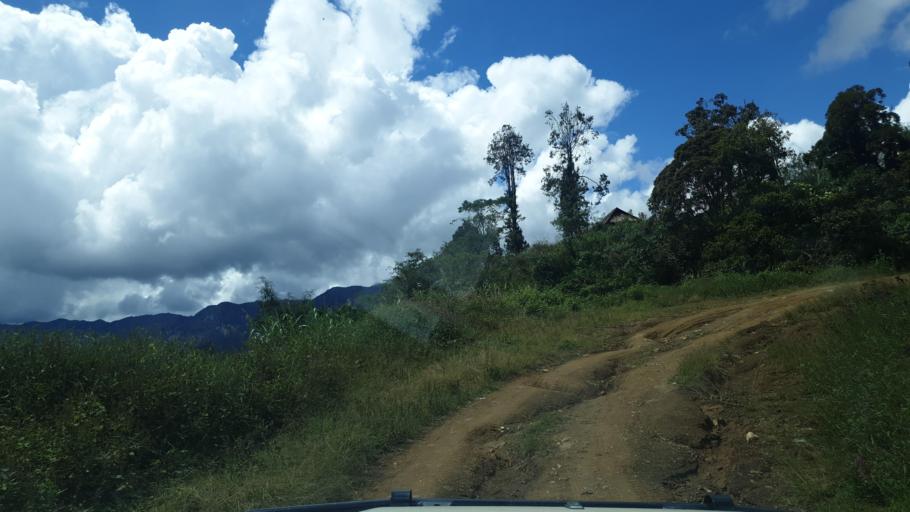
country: PG
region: Eastern Highlands
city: Goroka
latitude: -6.2761
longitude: 145.1872
